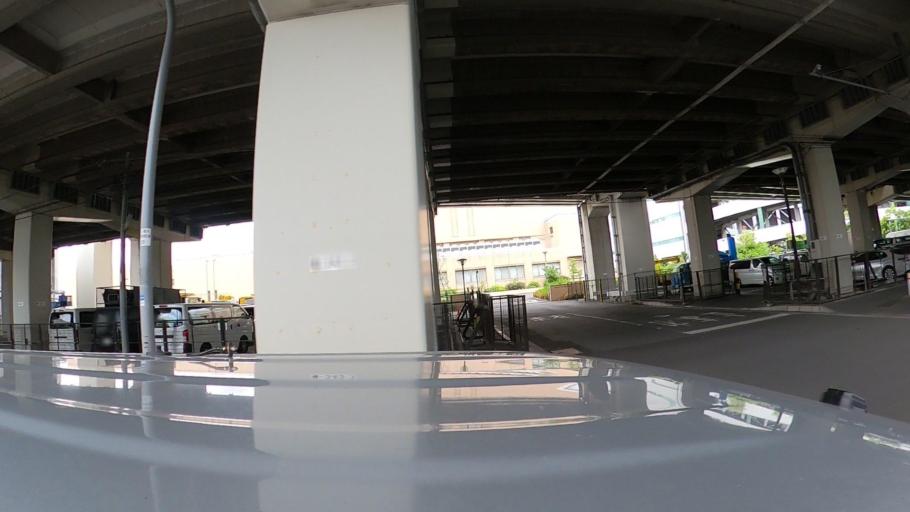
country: JP
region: Kanagawa
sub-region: Kawasaki-shi
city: Kawasaki
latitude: 35.4931
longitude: 139.6746
